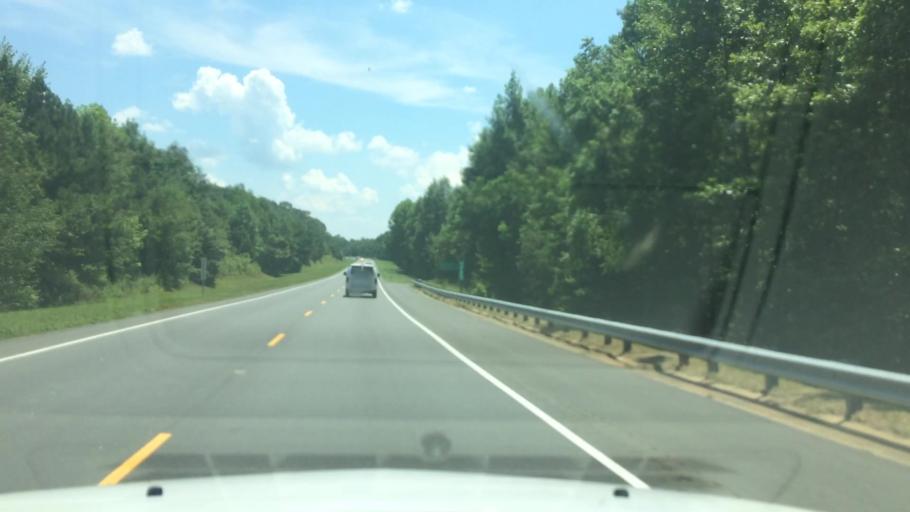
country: US
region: North Carolina
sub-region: Alexander County
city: Stony Point
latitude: 35.8311
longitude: -81.0158
